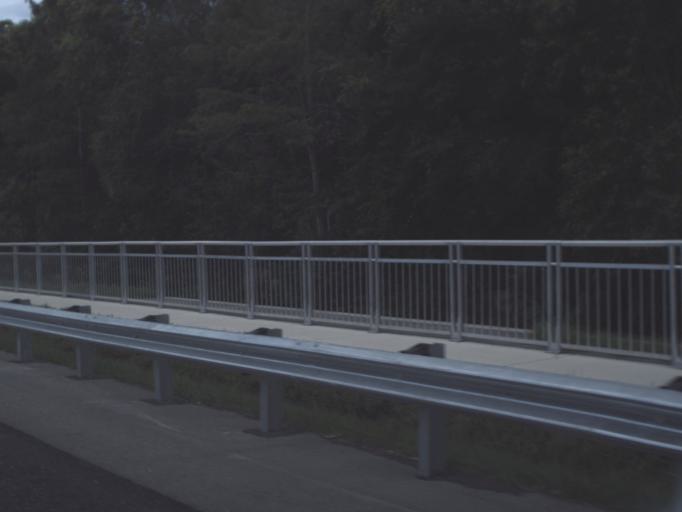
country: US
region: Florida
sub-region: Collier County
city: Lely Resort
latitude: 26.0479
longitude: -81.6750
